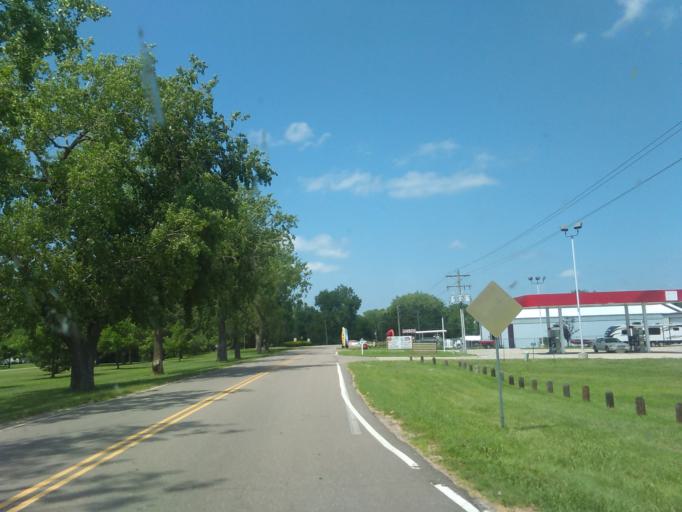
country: US
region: Nebraska
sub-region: Gosper County
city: Elwood
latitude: 40.6823
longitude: -99.8280
